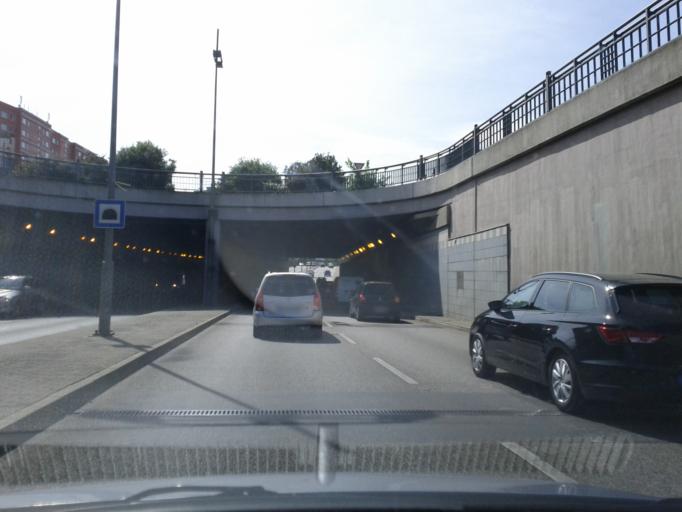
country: DE
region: Berlin
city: Friedrichsfelde
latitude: 52.5096
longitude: 13.5202
